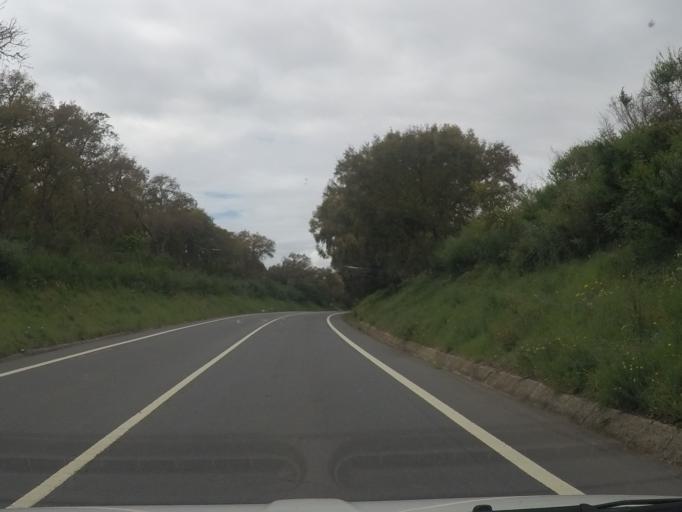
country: PT
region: Setubal
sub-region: Santiago do Cacem
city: Cercal
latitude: 37.8323
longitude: -8.7021
